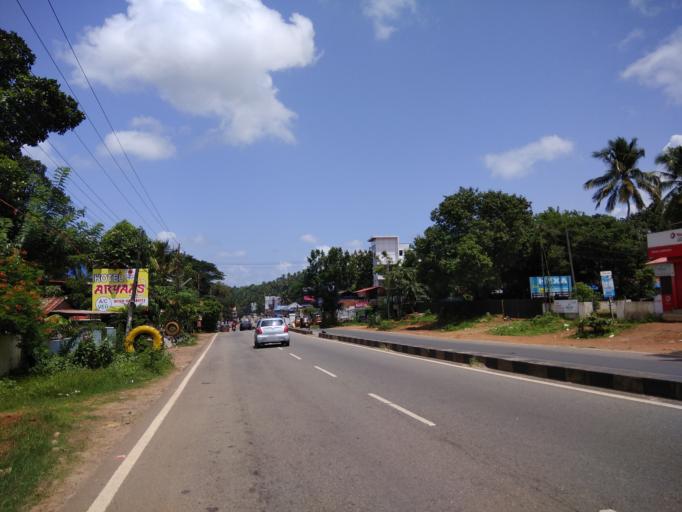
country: IN
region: Kerala
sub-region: Thrissur District
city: Avanoor
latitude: 10.5543
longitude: 76.1738
